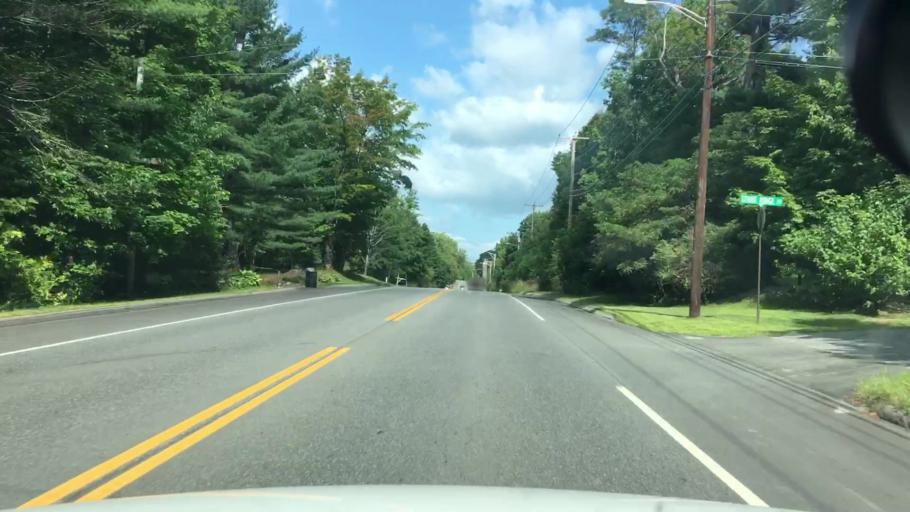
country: US
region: Maine
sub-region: Kennebec County
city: Waterville
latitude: 44.5797
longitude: -69.6464
